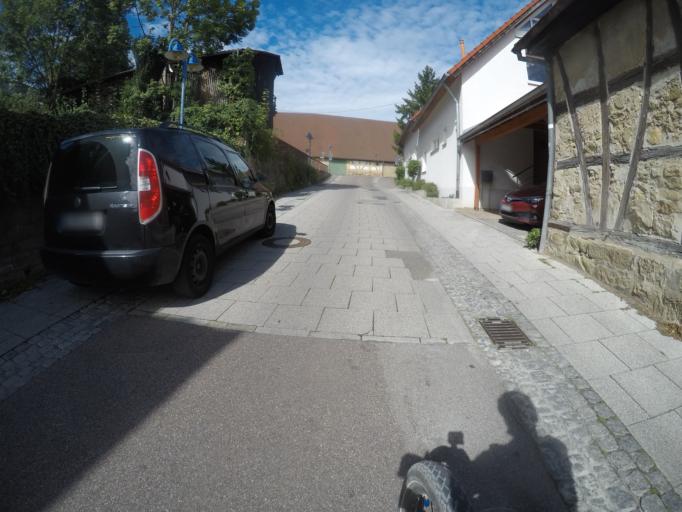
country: DE
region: Baden-Wuerttemberg
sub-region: Regierungsbezirk Stuttgart
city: Asperg
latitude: 48.9072
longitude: 9.1338
